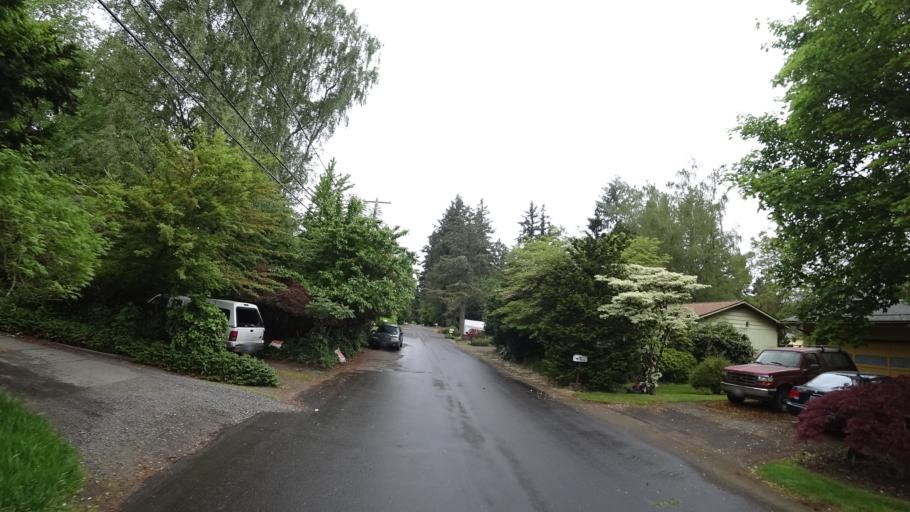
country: US
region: Oregon
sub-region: Washington County
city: Garden Home-Whitford
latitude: 45.4667
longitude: -122.7579
